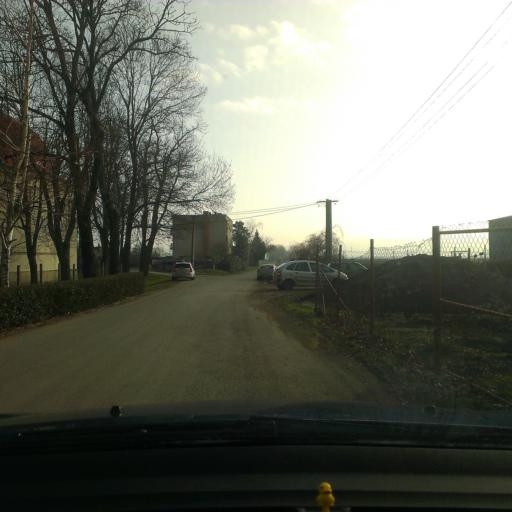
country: SK
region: Trnavsky
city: Leopoldov
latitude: 48.5221
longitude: 17.7673
